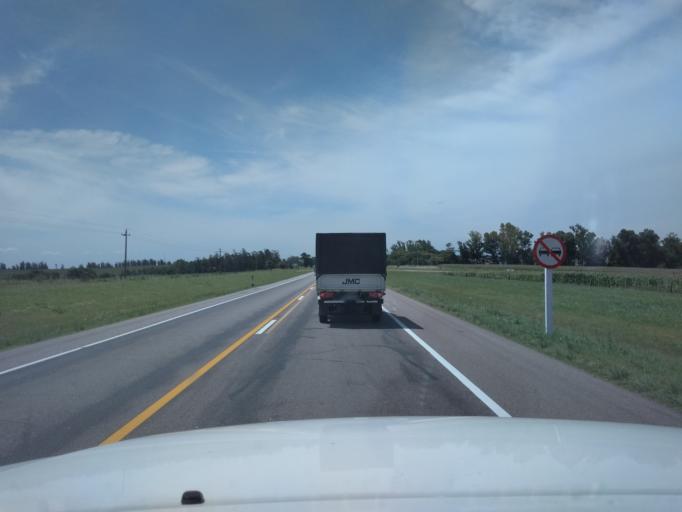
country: UY
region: Florida
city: Florida
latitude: -34.1362
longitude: -56.1833
